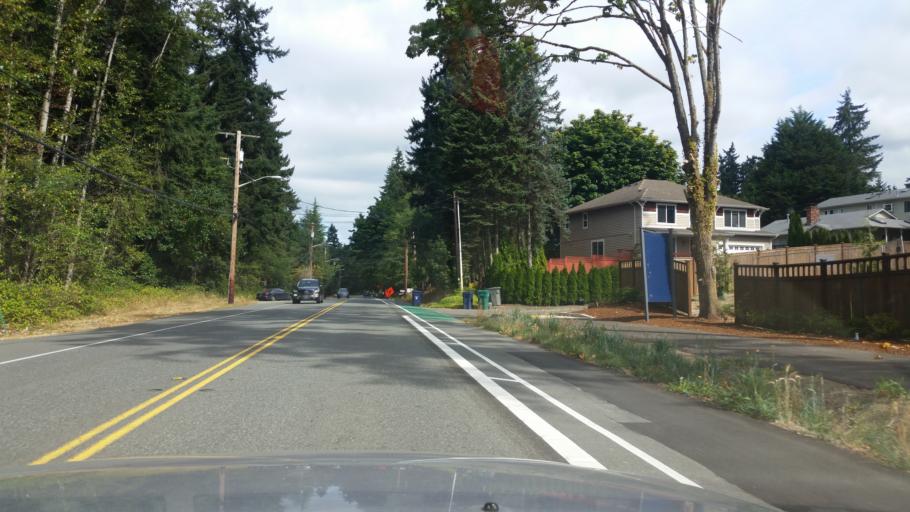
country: US
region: Washington
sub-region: King County
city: Inglewood-Finn Hill
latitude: 47.7129
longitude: -122.2376
